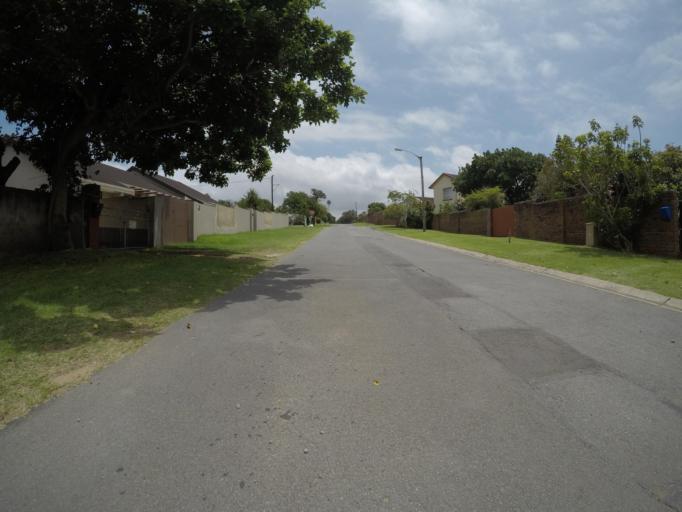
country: ZA
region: Eastern Cape
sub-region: Buffalo City Metropolitan Municipality
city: East London
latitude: -32.9449
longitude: 28.0187
